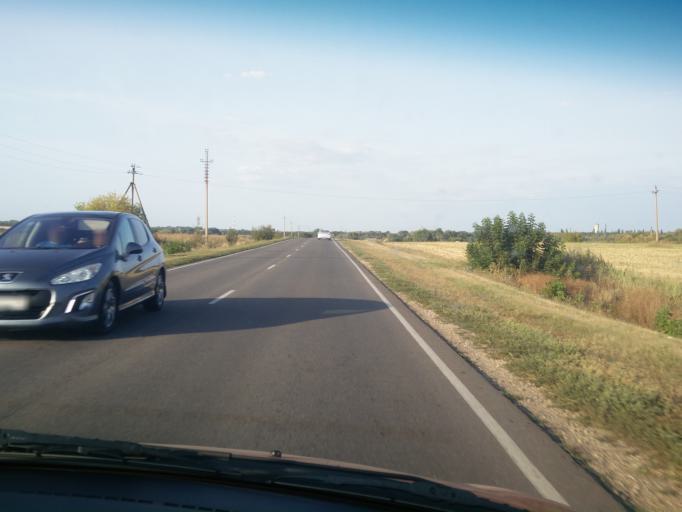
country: RU
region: Voronezj
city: Ramon'
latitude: 51.9320
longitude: 39.3308
